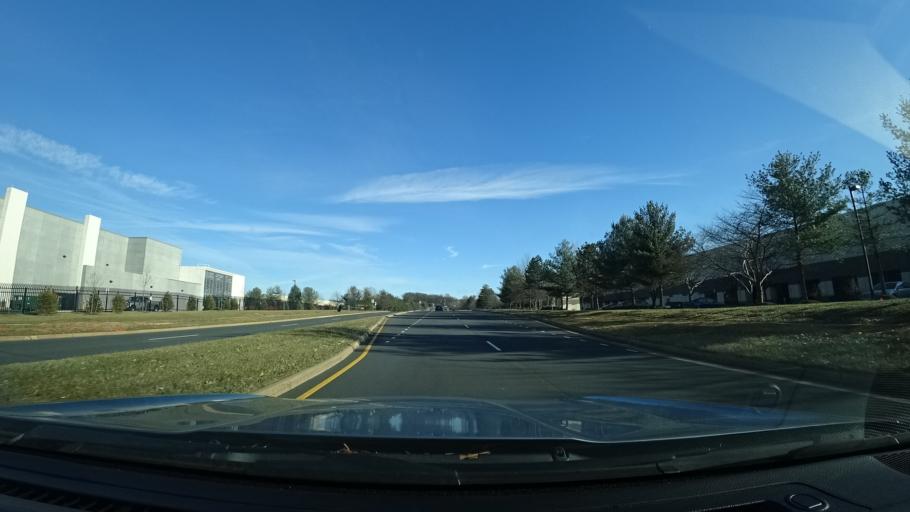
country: US
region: Virginia
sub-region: Loudoun County
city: Dulles Town Center
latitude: 39.0247
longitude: -77.4157
